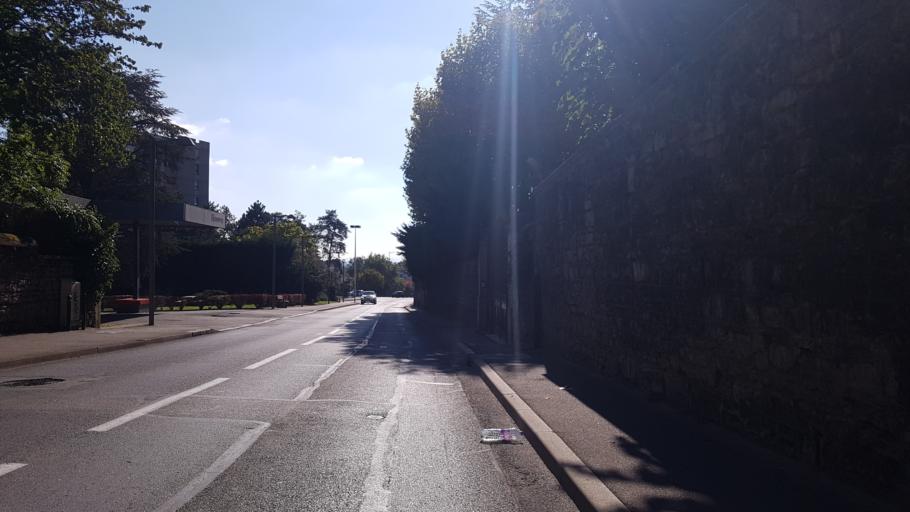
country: FR
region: Rhone-Alpes
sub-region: Departement du Rhone
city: Ecully
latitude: 45.7922
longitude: 4.7911
